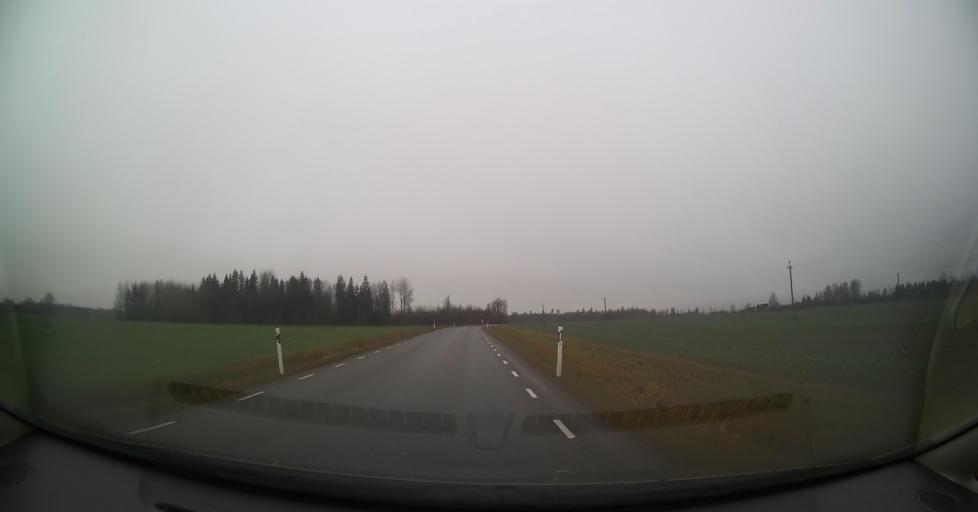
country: EE
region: Tartu
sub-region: Tartu linn
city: Tartu
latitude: 58.3982
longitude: 26.8643
